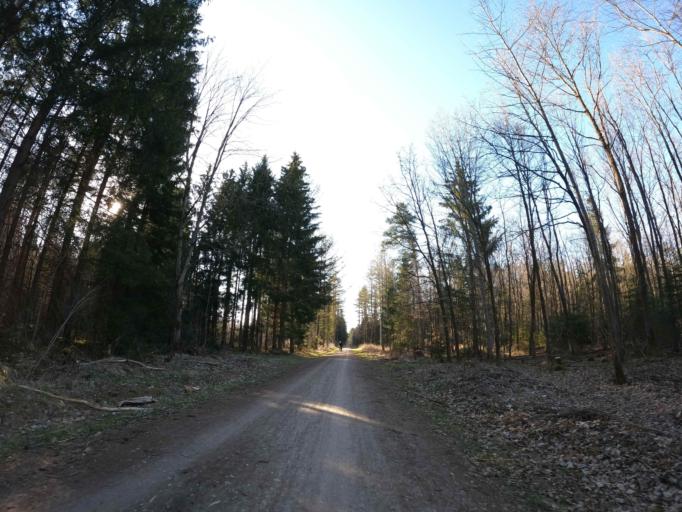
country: DE
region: Bavaria
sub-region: Upper Bavaria
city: Unterhaching
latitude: 48.0736
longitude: 11.5839
